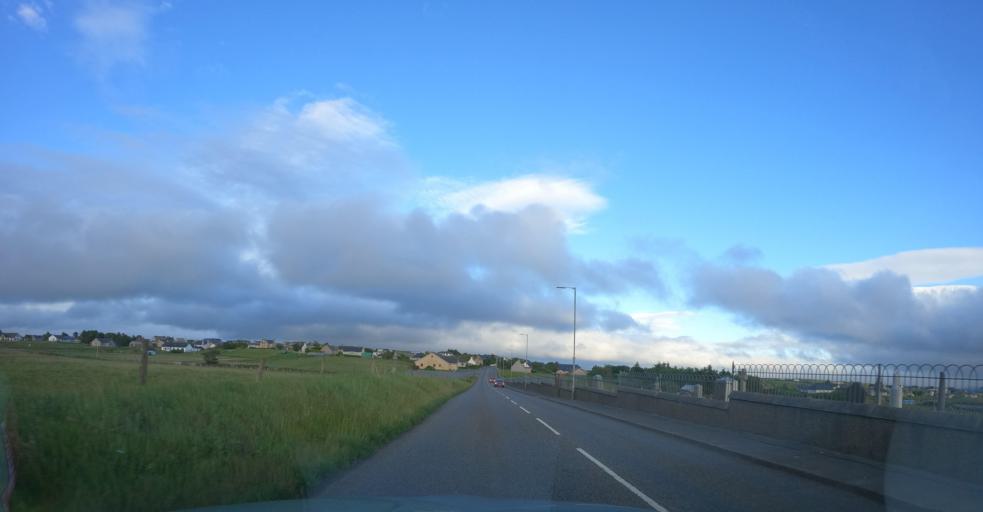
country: GB
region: Scotland
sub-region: Eilean Siar
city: Stornoway
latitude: 58.2073
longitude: -6.3592
